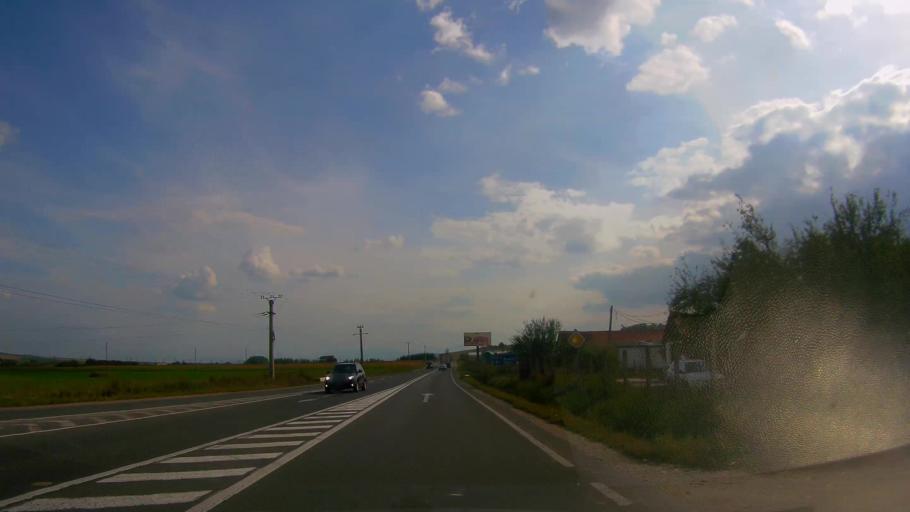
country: RO
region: Brasov
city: Maierus
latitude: 45.8938
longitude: 25.5351
